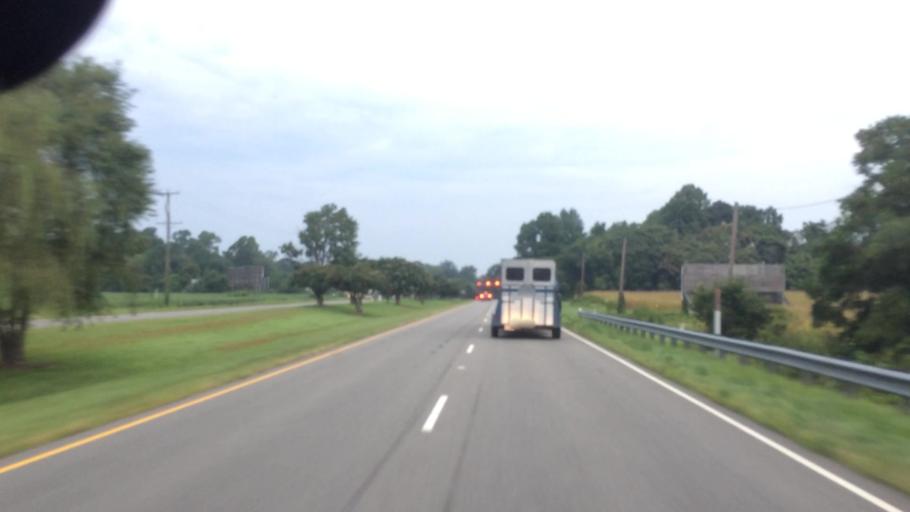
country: US
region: Virginia
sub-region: King William County
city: West Point
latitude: 37.3988
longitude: -76.8067
